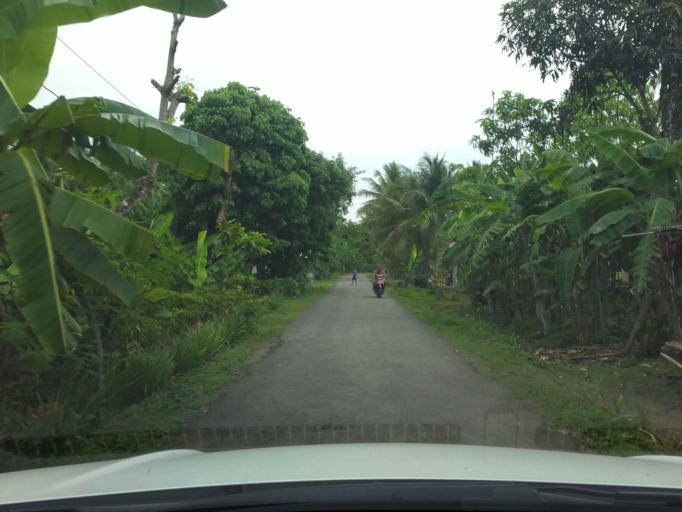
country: ID
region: West Java
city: Sarimukti Kaler
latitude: -7.4218
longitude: 108.7237
